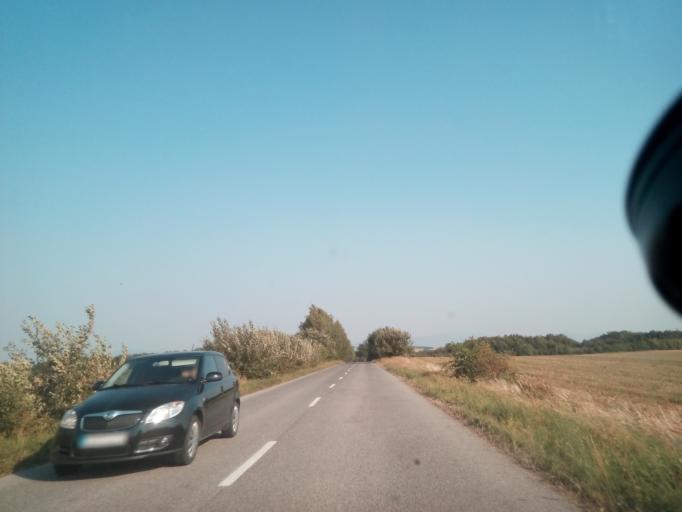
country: SK
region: Kosicky
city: Kosice
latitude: 48.7266
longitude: 21.1224
